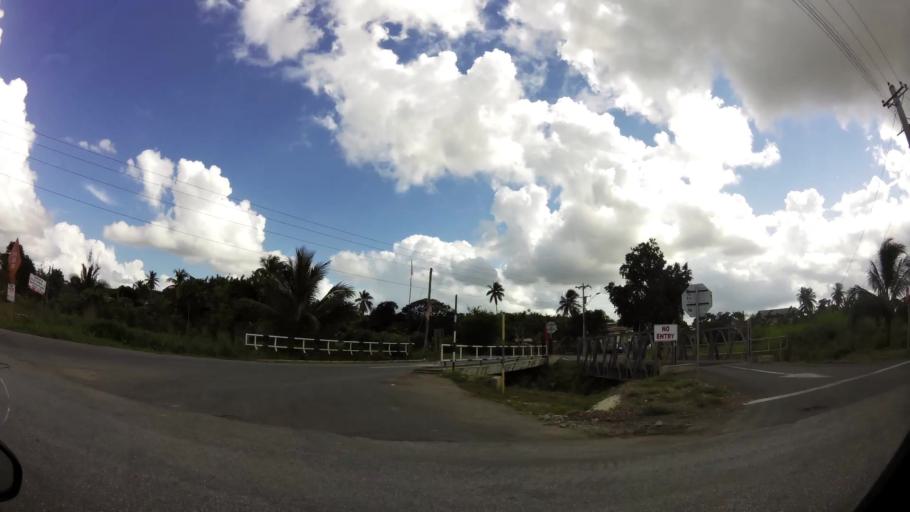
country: TT
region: Penal/Debe
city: Debe
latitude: 10.2256
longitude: -61.4374
